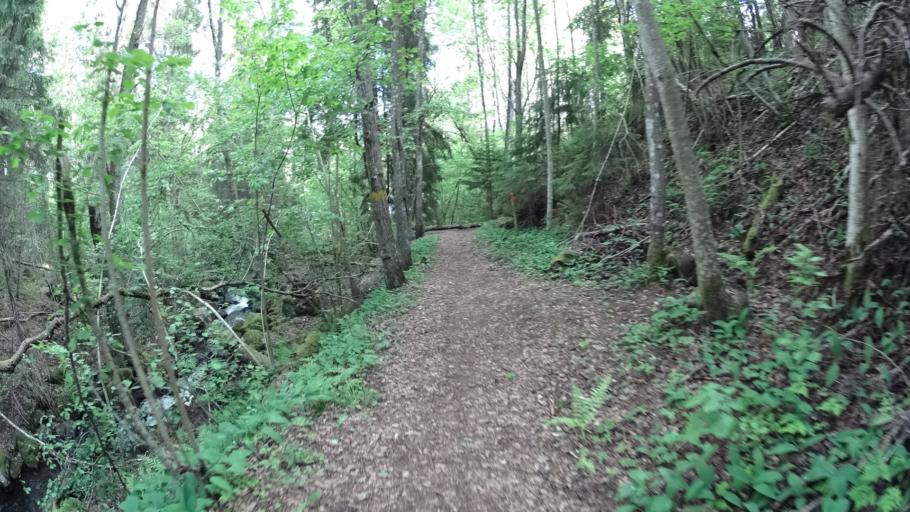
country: FI
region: Uusimaa
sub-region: Raaseporin
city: Pohja
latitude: 60.1454
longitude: 23.5409
